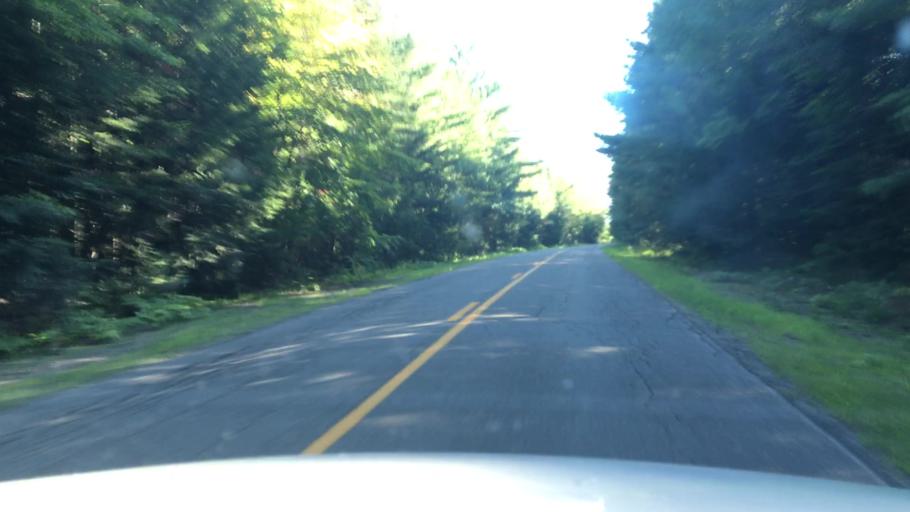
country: US
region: Maine
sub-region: Penobscot County
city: Enfield
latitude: 45.2135
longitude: -68.5873
